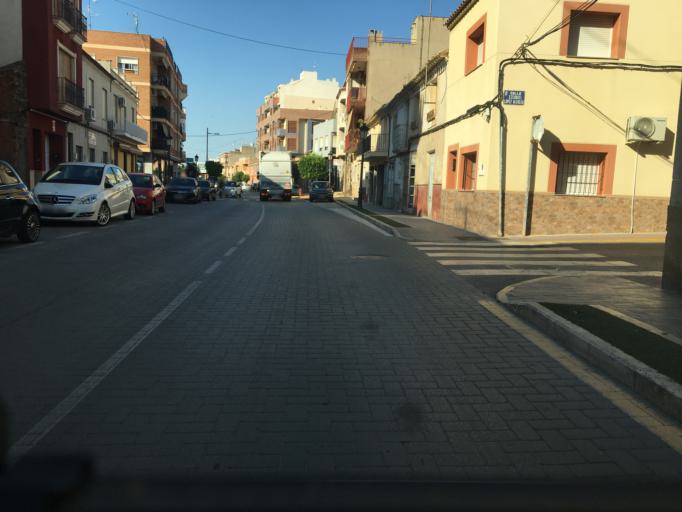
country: ES
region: Murcia
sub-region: Murcia
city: Puerto Lumbreras
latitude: 37.5589
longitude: -1.8110
